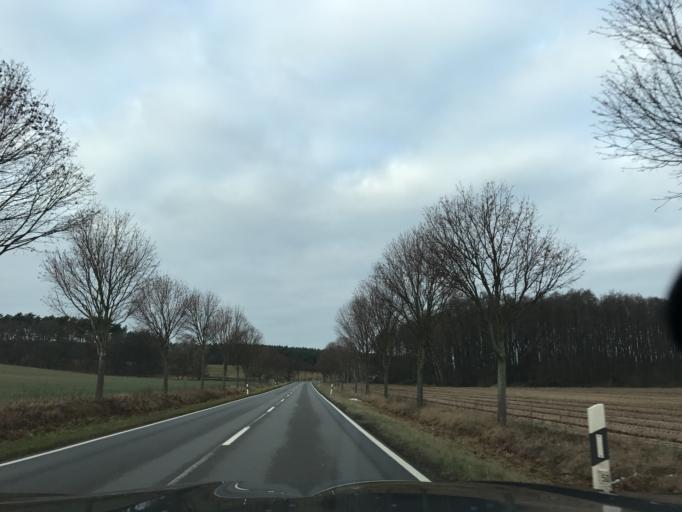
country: DE
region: Brandenburg
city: Golzow
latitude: 52.3520
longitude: 12.6147
